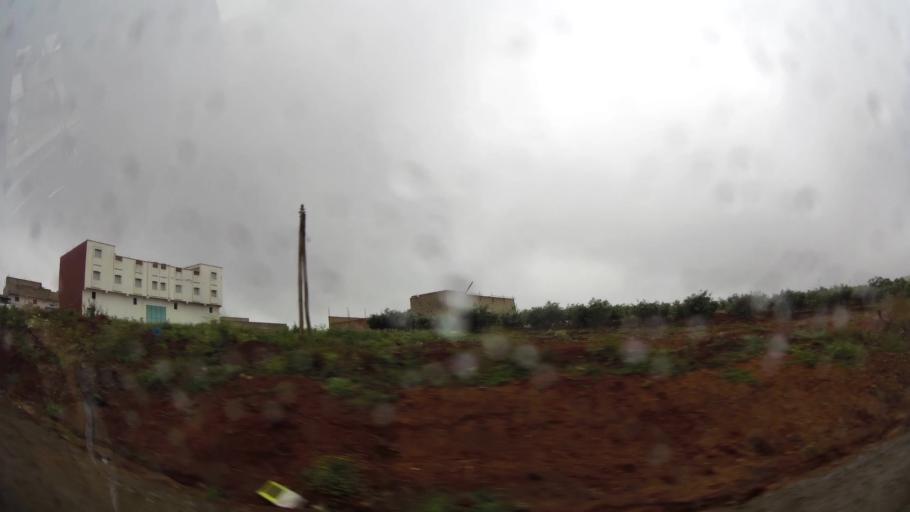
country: MA
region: Oriental
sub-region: Nador
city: Boudinar
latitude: 35.1252
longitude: -3.6288
